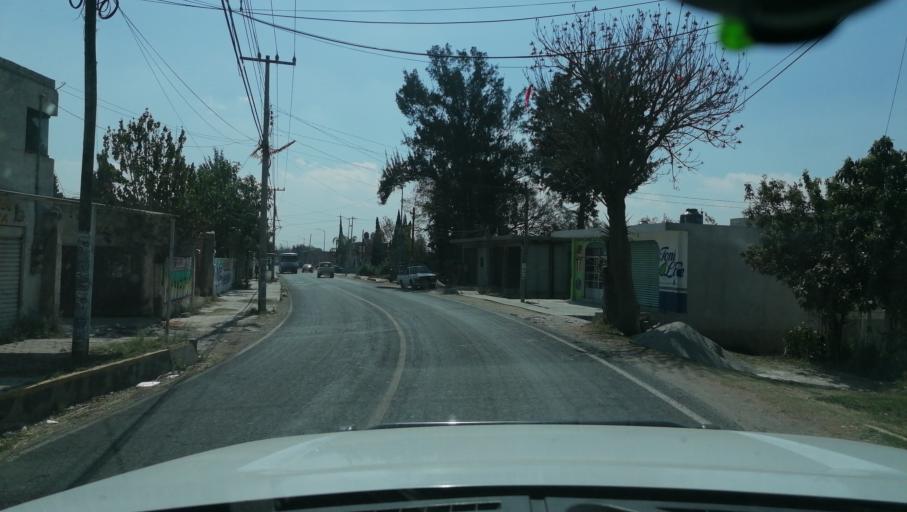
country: MX
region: Tlaxcala
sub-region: Tetlatlahuca
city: Tetlatlahuca
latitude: 19.2332
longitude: -98.3009
